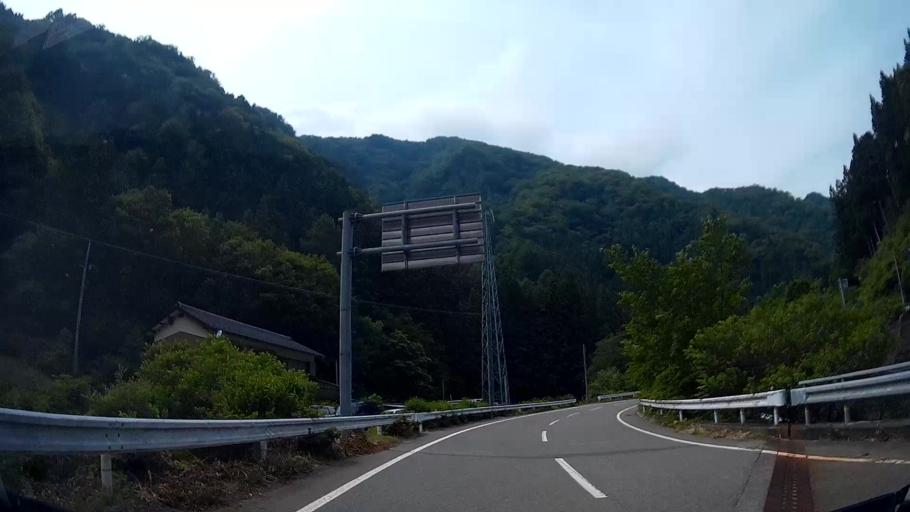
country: JP
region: Nagano
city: Iida
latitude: 35.4411
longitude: 137.9912
